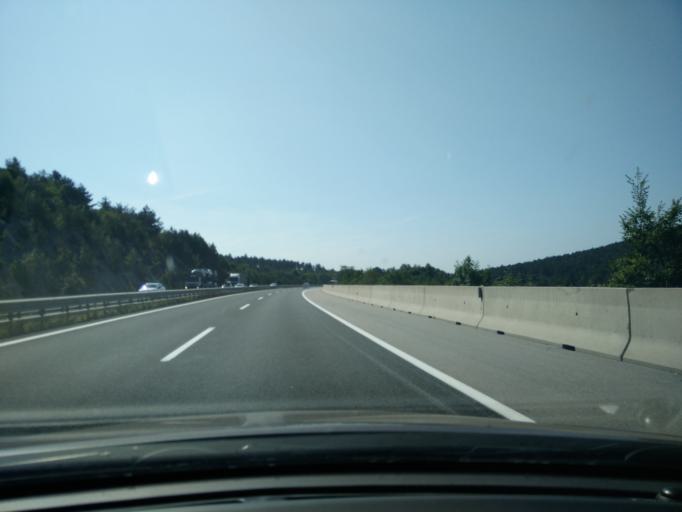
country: SI
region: Divaca
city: Divaca
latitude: 45.7106
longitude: 14.0019
